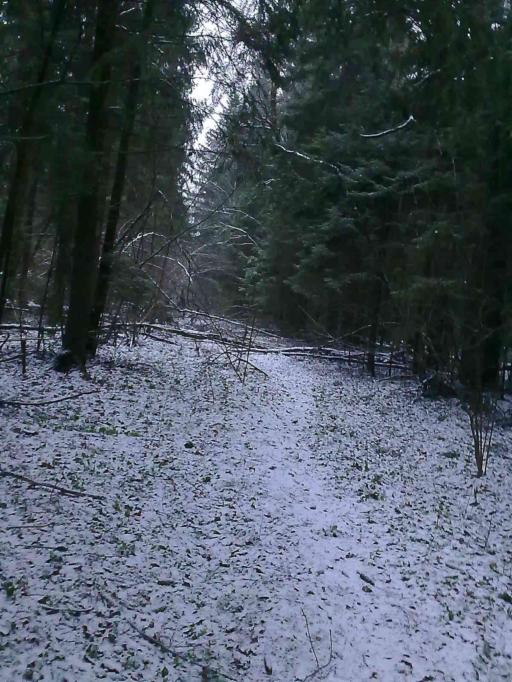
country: RU
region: Moskovskaya
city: Lesnoy Gorodok
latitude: 55.6592
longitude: 37.1594
